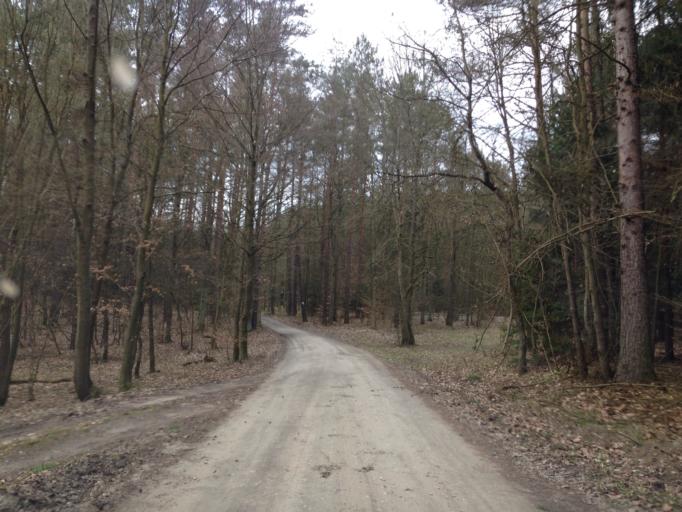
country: PL
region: Kujawsko-Pomorskie
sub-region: Powiat brodnicki
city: Gorzno
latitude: 53.2235
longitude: 19.7243
